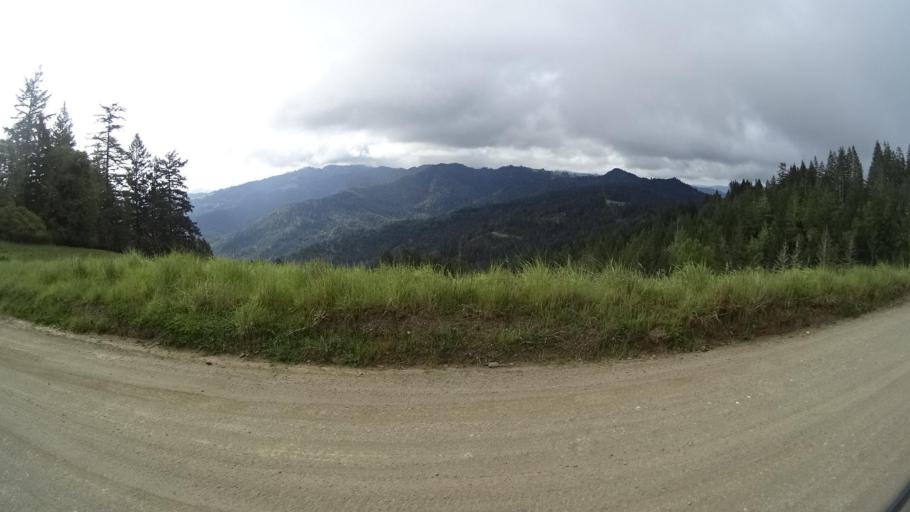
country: US
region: California
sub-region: Humboldt County
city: Redway
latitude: 40.2539
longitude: -123.7643
